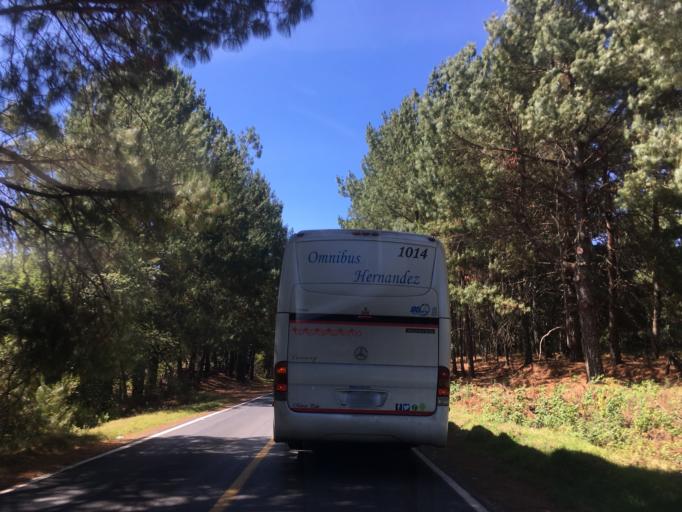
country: MX
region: Michoacan
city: Tzitzio
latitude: 19.6809
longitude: -100.8656
